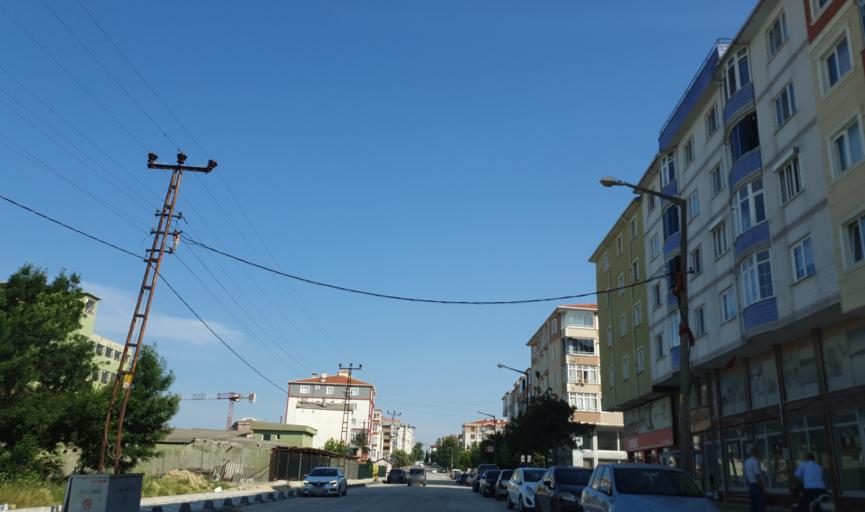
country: TR
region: Tekirdag
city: Saray
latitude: 41.4463
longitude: 27.9160
